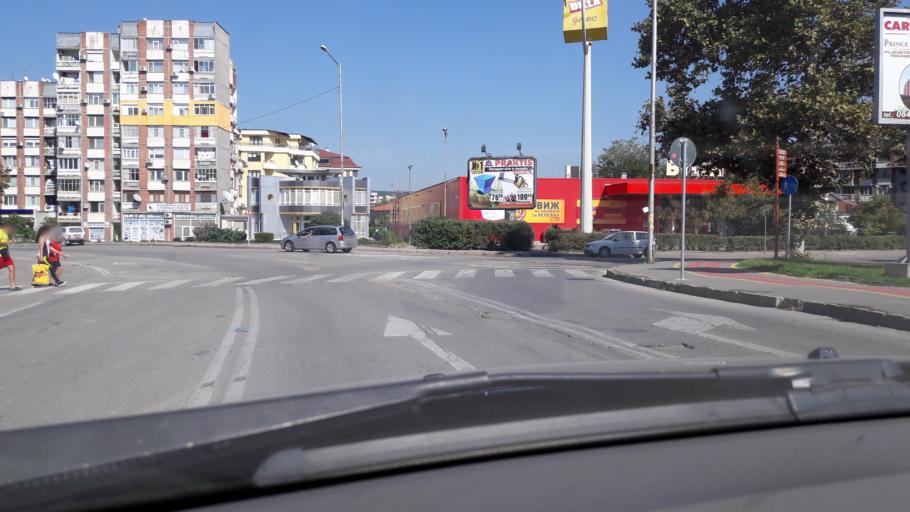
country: BG
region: Razgrad
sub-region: Obshtina Razgrad
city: Razgrad
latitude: 43.5290
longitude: 26.5199
